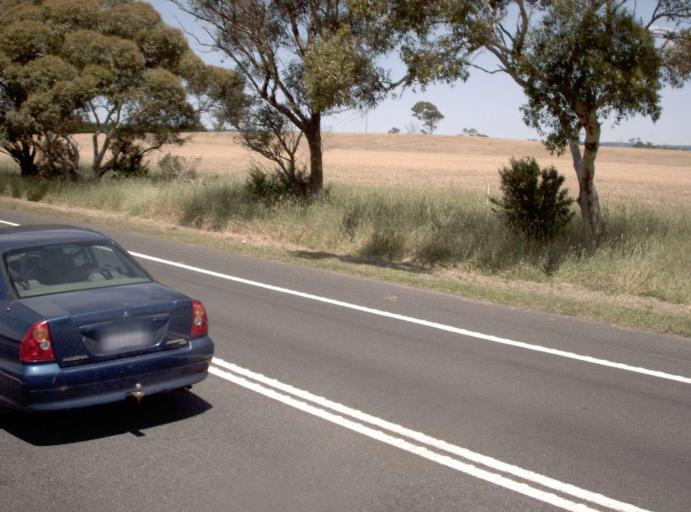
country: AU
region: Victoria
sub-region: Latrobe
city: Traralgon
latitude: -38.1580
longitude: 146.7168
